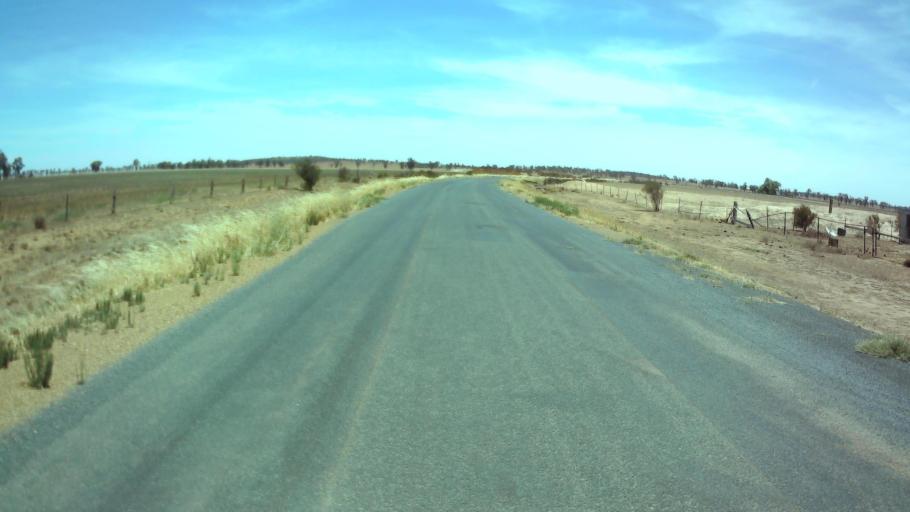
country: AU
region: New South Wales
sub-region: Weddin
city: Grenfell
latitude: -33.7504
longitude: 147.7669
